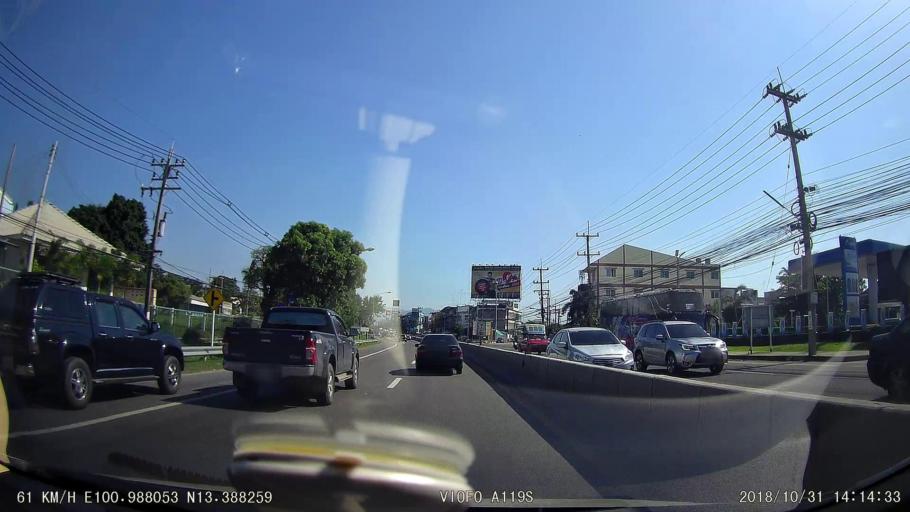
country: TH
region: Chon Buri
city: Chon Buri
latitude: 13.3881
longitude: 100.9881
